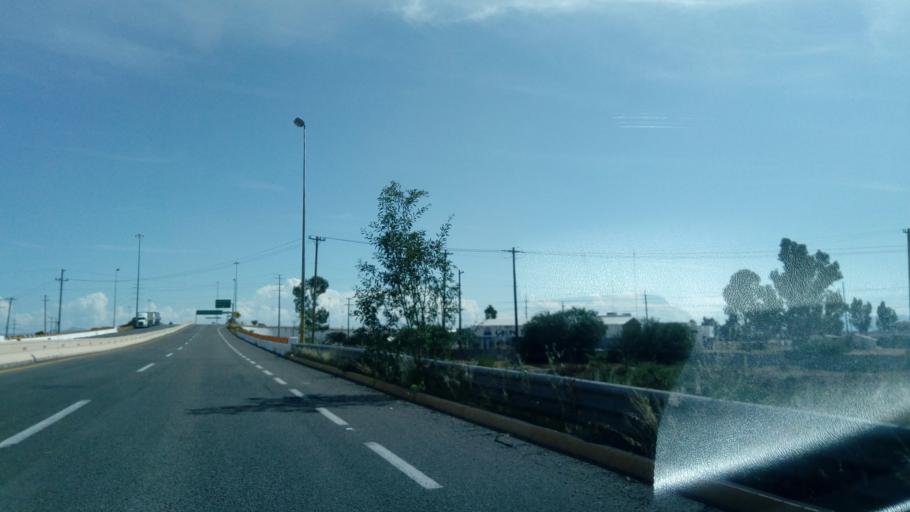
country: MX
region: Durango
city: Victoria de Durango
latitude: 24.0940
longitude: -104.5805
